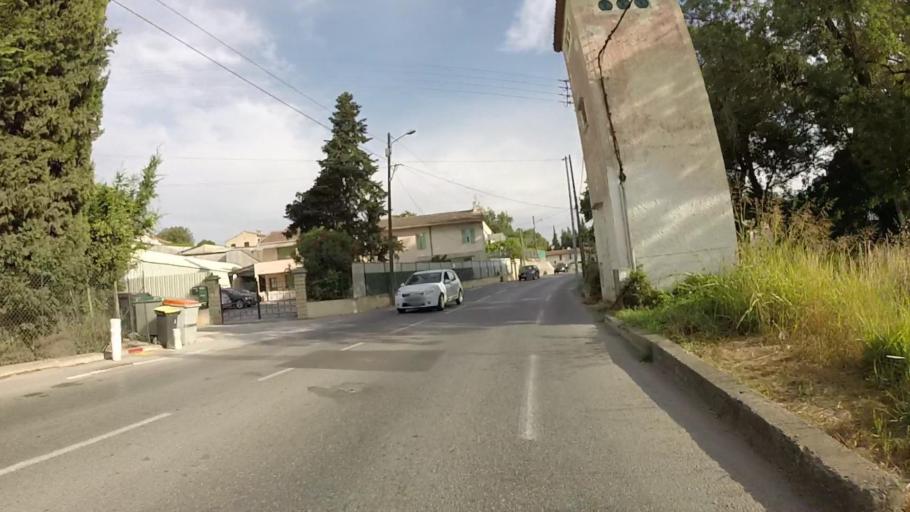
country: FR
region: Provence-Alpes-Cote d'Azur
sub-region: Departement des Alpes-Maritimes
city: Biot
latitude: 43.6092
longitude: 7.1104
